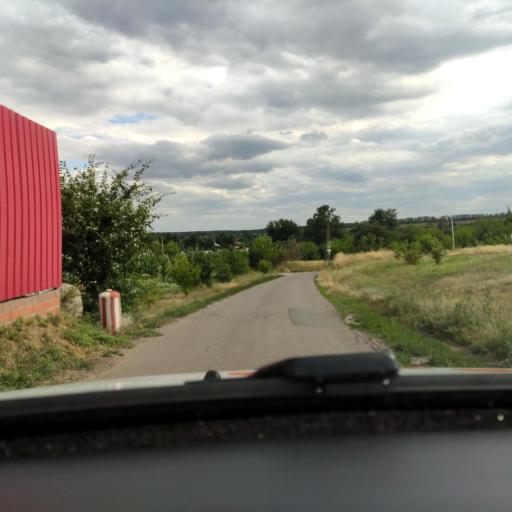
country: RU
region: Voronezj
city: Orlovo
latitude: 51.6518
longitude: 39.5712
